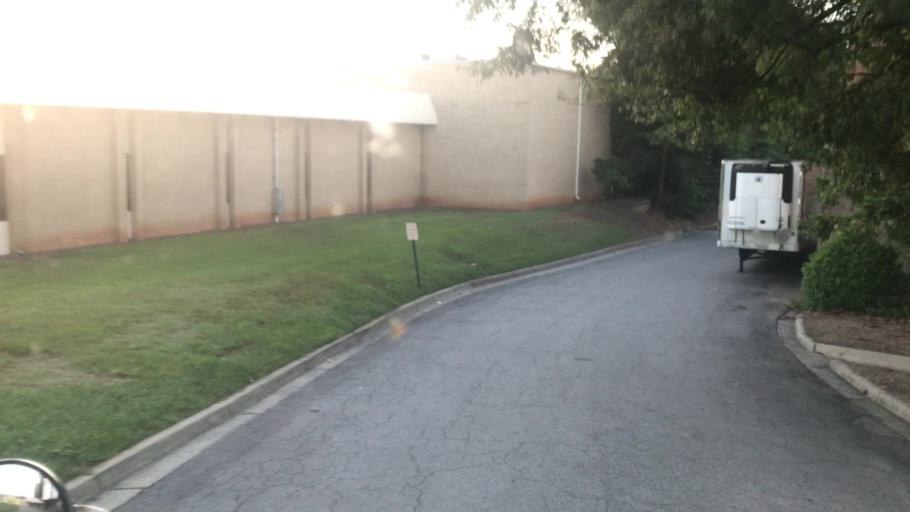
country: US
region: Georgia
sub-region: DeKalb County
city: Doraville
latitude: 33.9292
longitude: -84.2649
